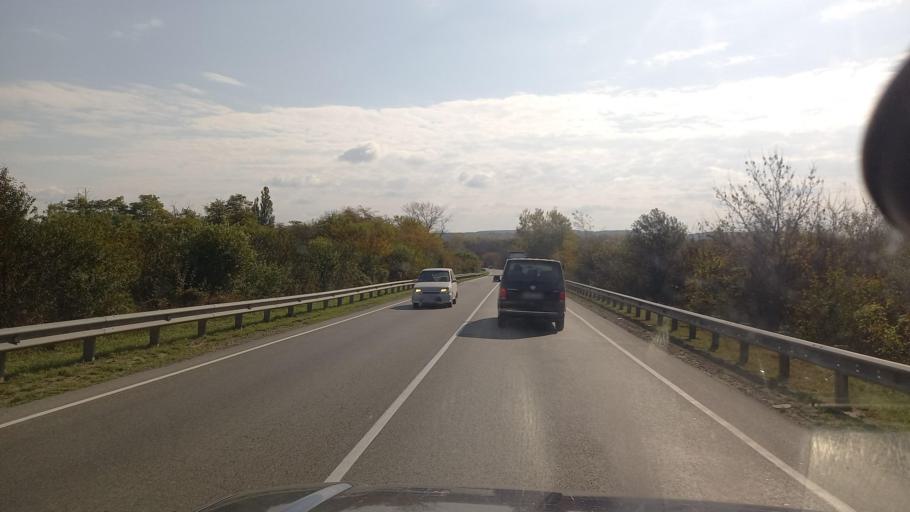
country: RU
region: Krasnodarskiy
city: Abinsk
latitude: 44.8463
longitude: 38.1494
